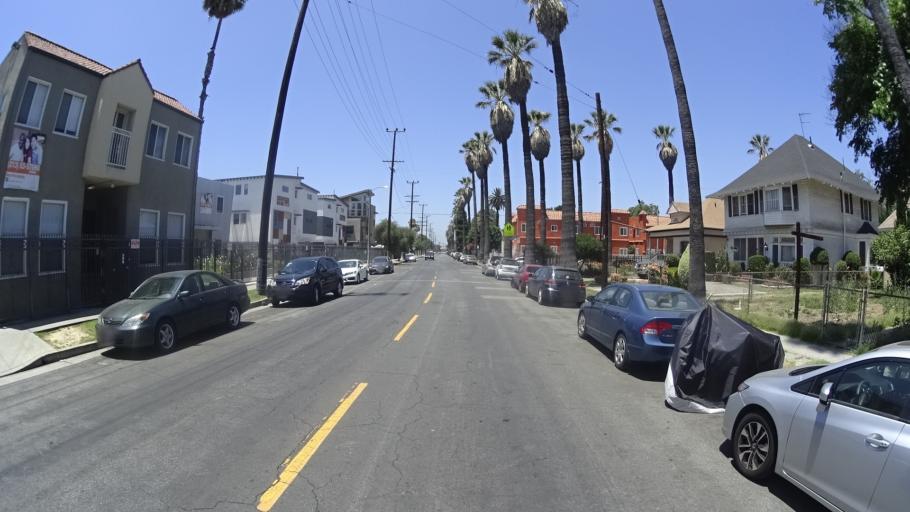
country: US
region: California
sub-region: Los Angeles County
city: Los Angeles
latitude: 34.0221
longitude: -118.2933
